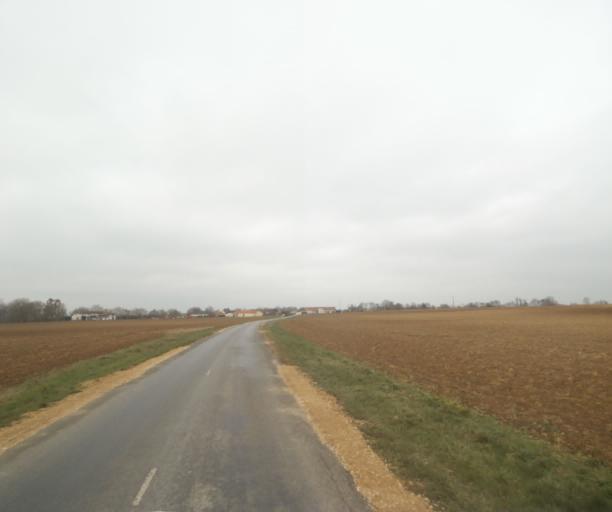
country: FR
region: Champagne-Ardenne
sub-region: Departement de la Marne
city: Pargny-sur-Saulx
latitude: 48.6891
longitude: 4.8097
